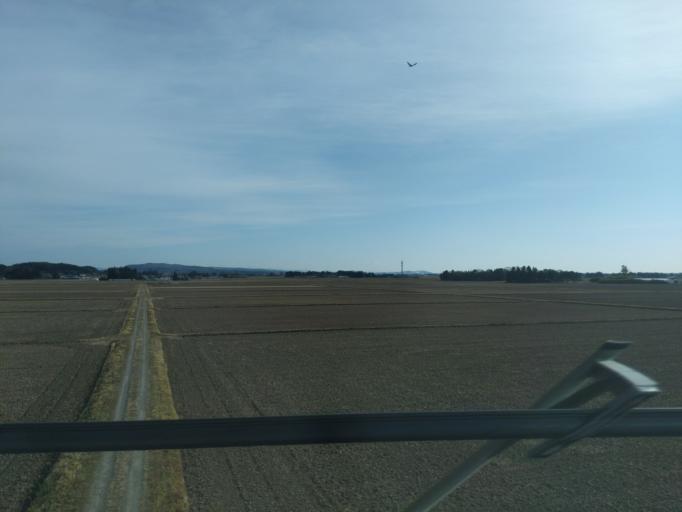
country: JP
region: Miyagi
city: Furukawa
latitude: 38.6107
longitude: 140.9900
